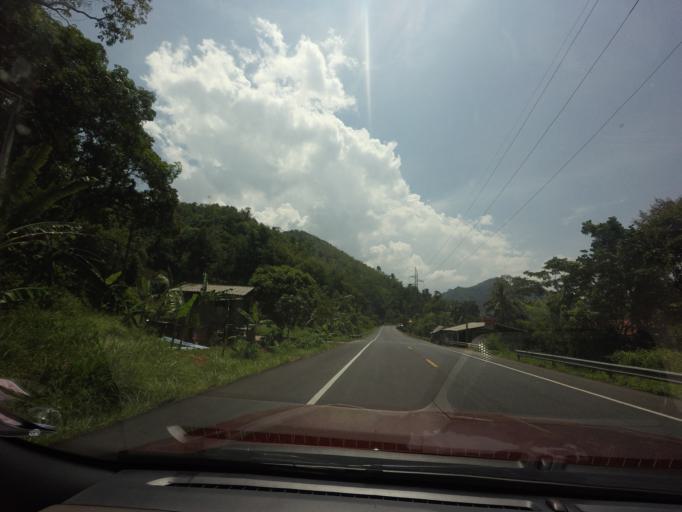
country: TH
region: Yala
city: Than To
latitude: 5.9702
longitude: 101.2007
